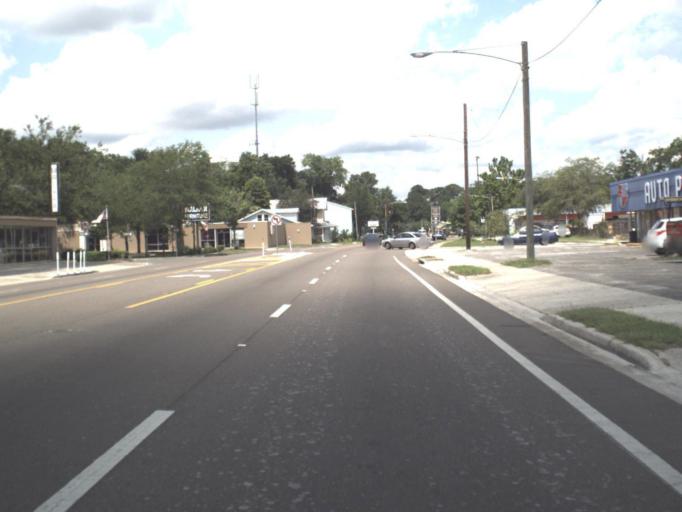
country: US
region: Florida
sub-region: Alachua County
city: Gainesville
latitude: 29.6592
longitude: -82.3258
